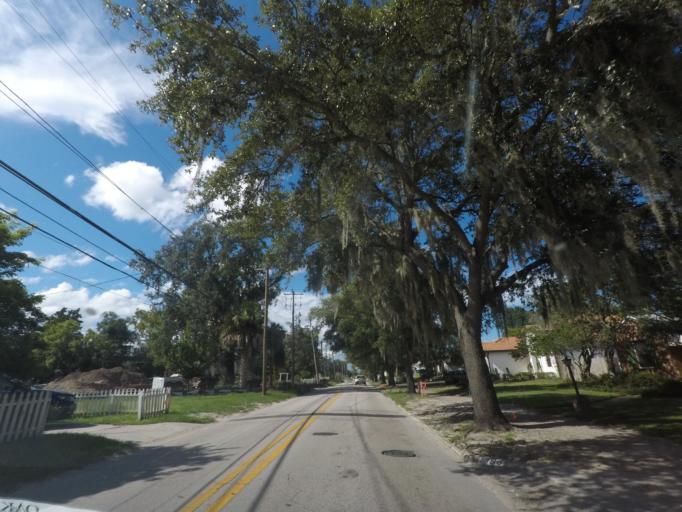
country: US
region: Florida
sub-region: Orange County
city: Fairview Shores
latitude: 28.5845
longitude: -81.3732
